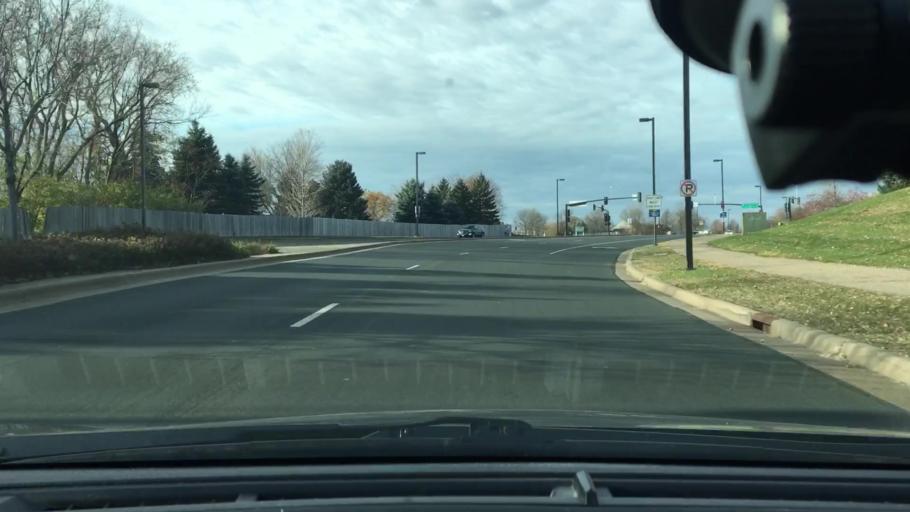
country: US
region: Minnesota
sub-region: Hennepin County
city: Maple Grove
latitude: 45.1031
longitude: -93.4661
